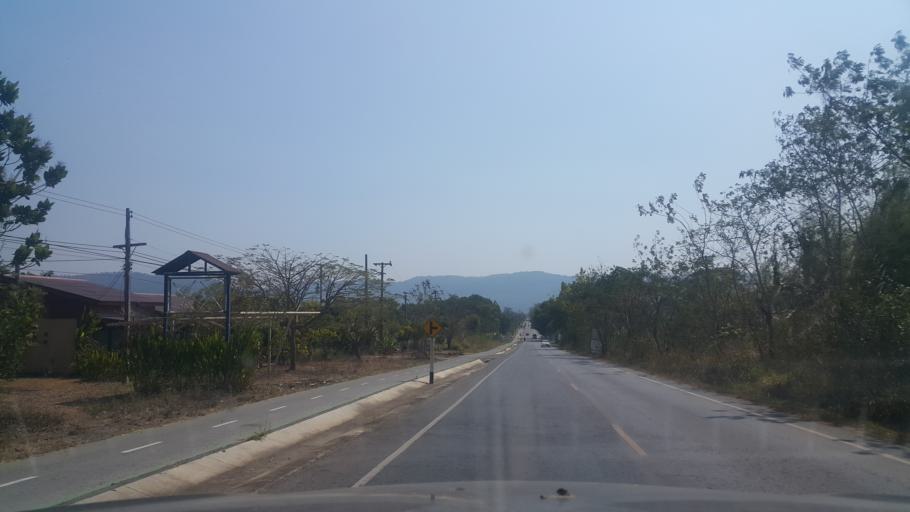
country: TH
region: Nakhon Ratchasima
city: Wang Nam Khiao
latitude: 14.3657
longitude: 101.9085
